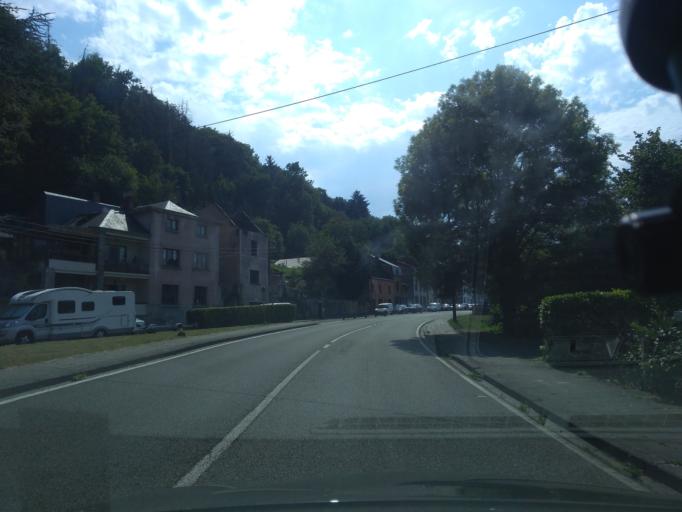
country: BE
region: Wallonia
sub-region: Province de Namur
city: Dinant
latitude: 50.2401
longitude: 4.9188
